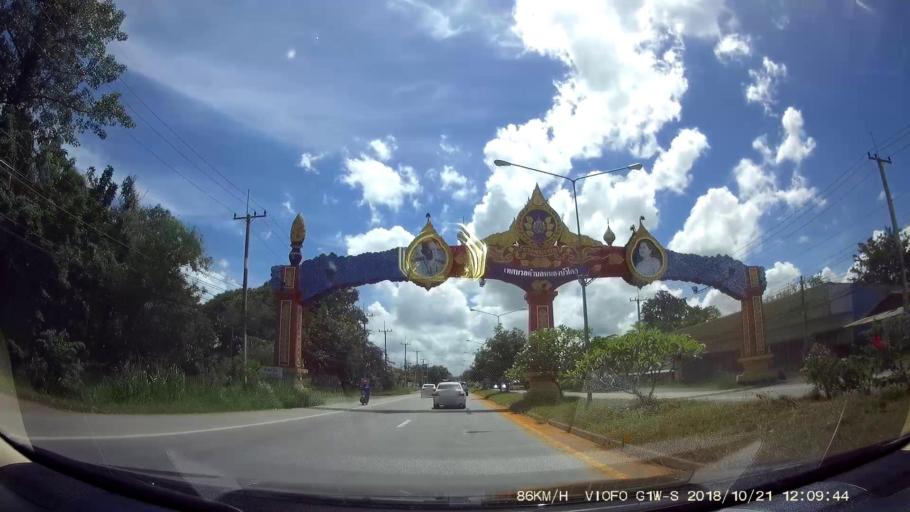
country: TH
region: Chaiyaphum
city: Chatturat
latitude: 15.4174
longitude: 101.8331
